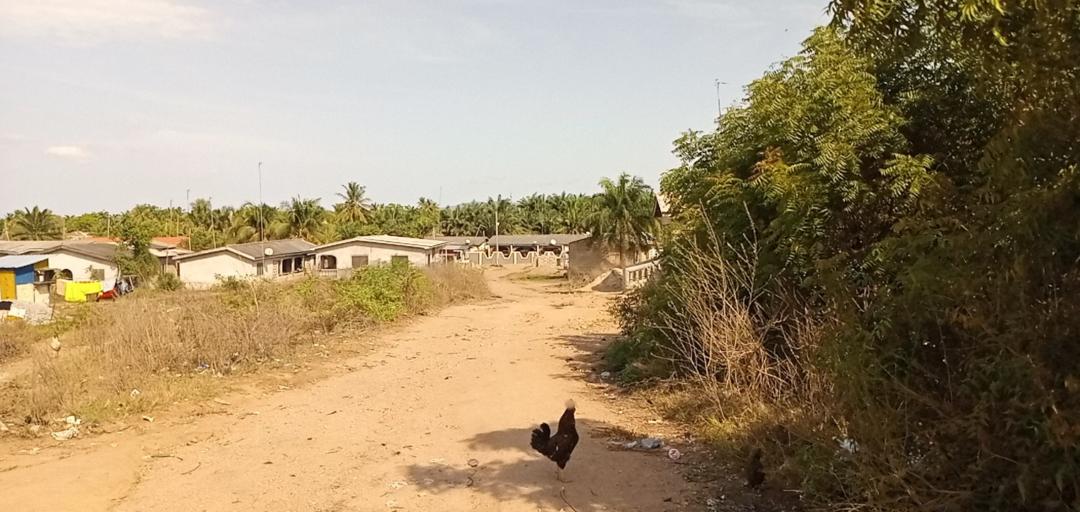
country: GH
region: Central
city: Winneba
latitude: 5.3529
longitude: -0.6218
